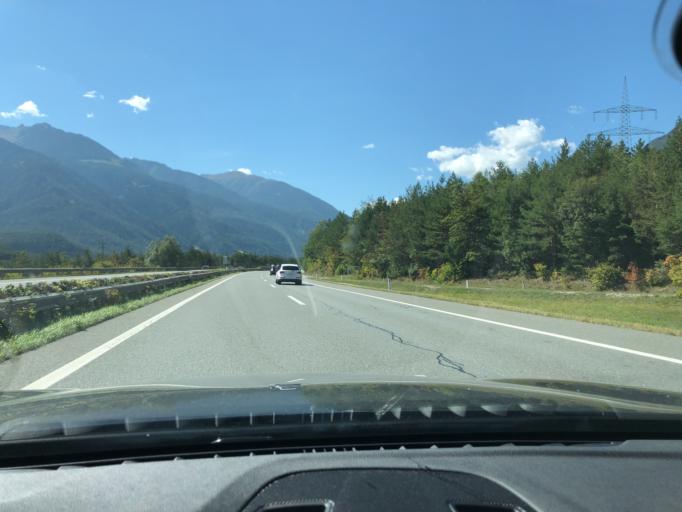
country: AT
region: Tyrol
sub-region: Politischer Bezirk Imst
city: Haiming
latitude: 47.2401
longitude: 10.8467
